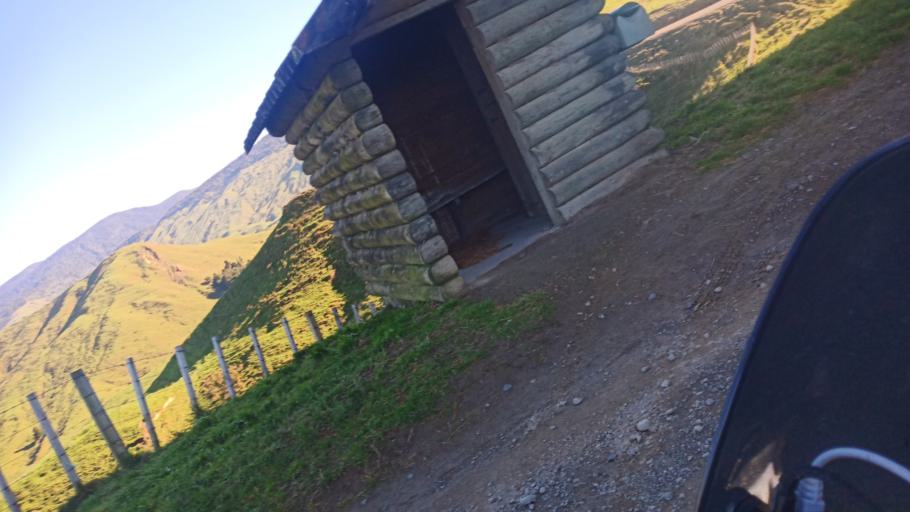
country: NZ
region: Hawke's Bay
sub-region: Wairoa District
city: Wairoa
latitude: -38.7858
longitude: 177.2708
